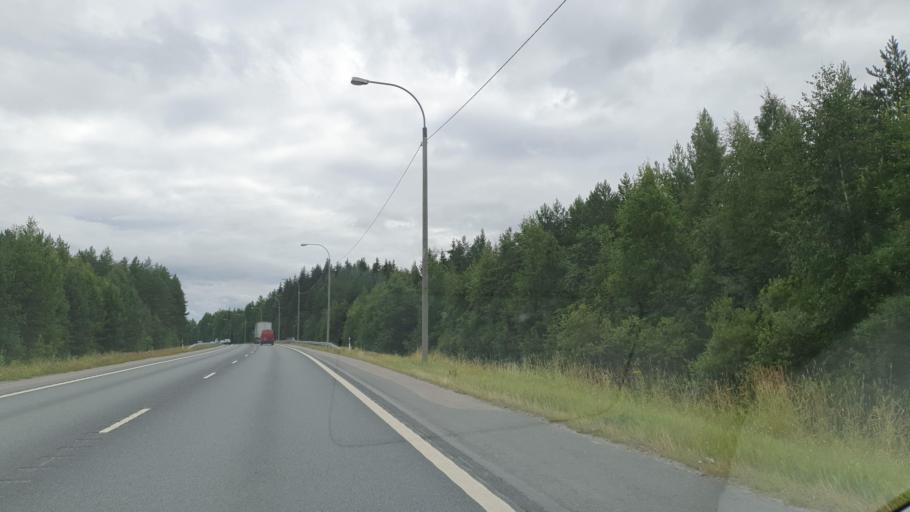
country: FI
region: Northern Savo
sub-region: Ylae-Savo
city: Iisalmi
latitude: 63.5122
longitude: 27.2568
